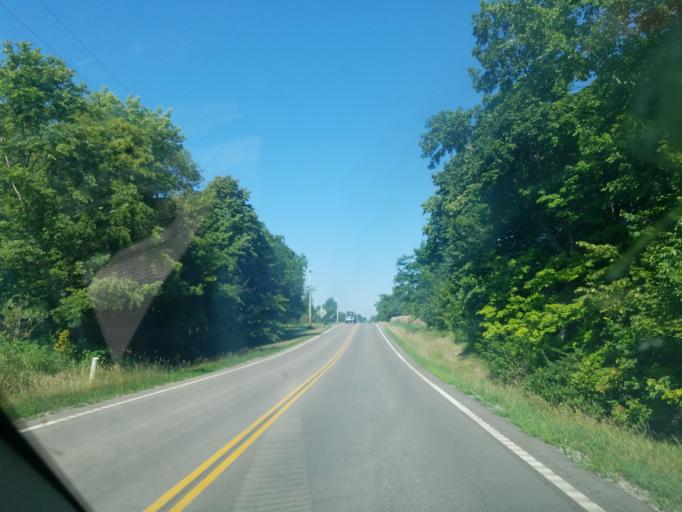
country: US
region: Ohio
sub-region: Logan County
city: Northwood
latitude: 40.4545
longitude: -83.7326
